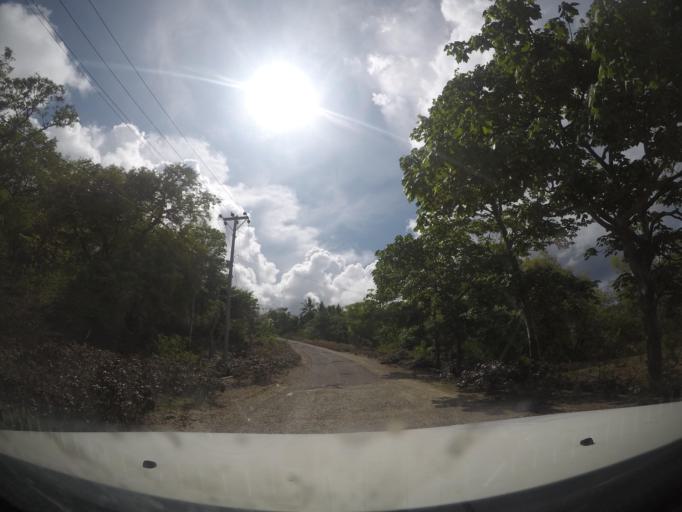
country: TL
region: Lautem
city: Lospalos
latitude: -8.3430
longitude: 127.0274
